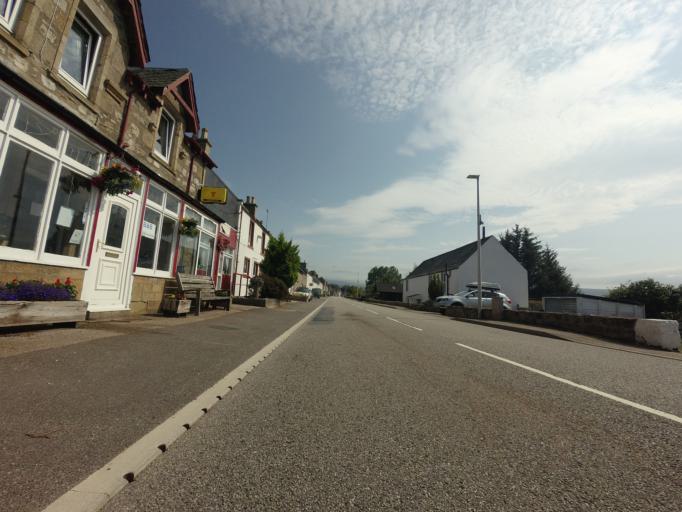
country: GB
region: Scotland
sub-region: Highland
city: Alness
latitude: 57.8949
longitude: -4.3481
